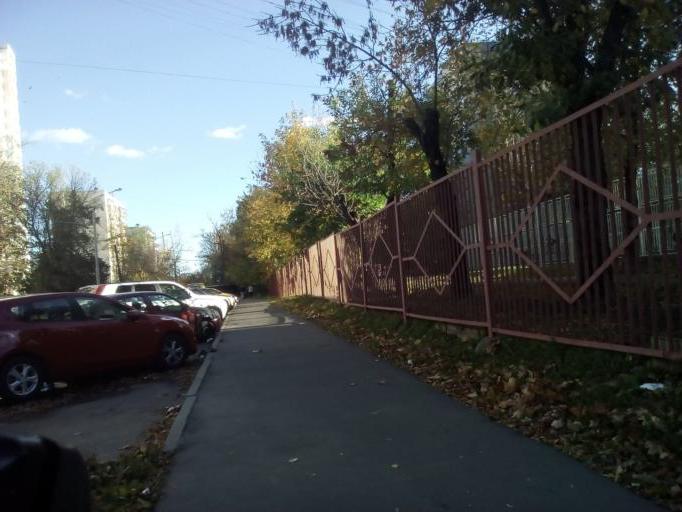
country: RU
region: Moscow
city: Likhobory
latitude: 55.8445
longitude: 37.5458
